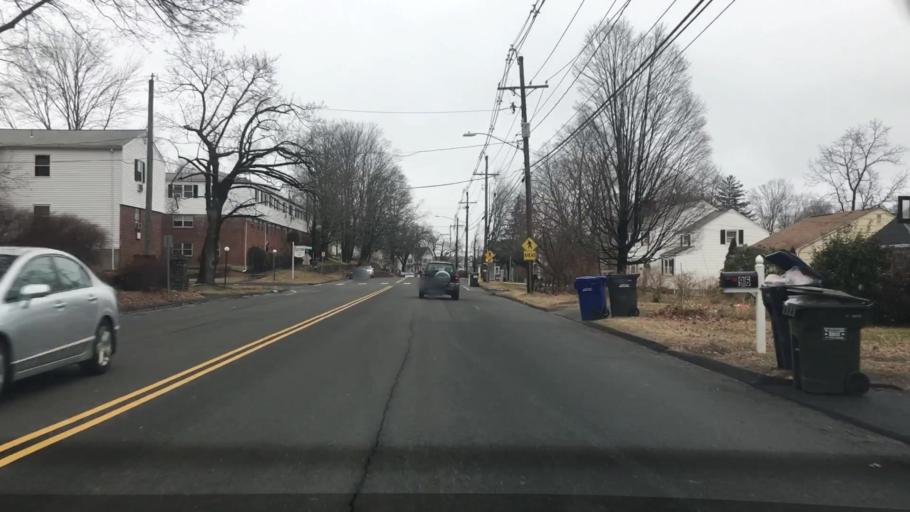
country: US
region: Connecticut
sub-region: Fairfield County
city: Danbury
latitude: 41.3838
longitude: -73.4605
